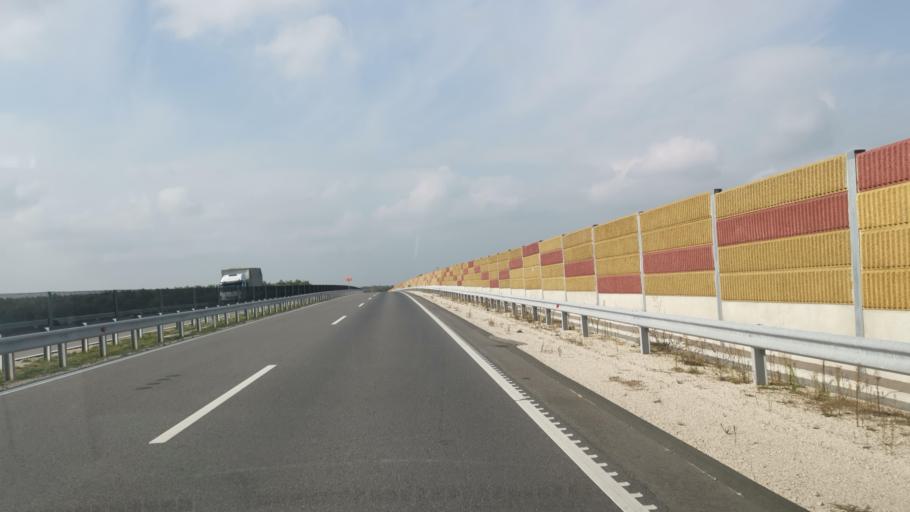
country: HU
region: Gyor-Moson-Sopron
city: Kapuvar
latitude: 47.5815
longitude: 16.9804
